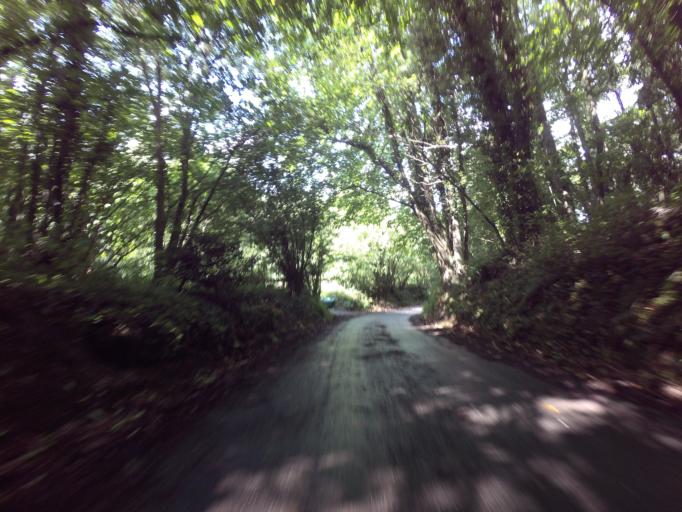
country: GB
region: England
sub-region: Kent
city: Borough Green
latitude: 51.2668
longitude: 0.2914
